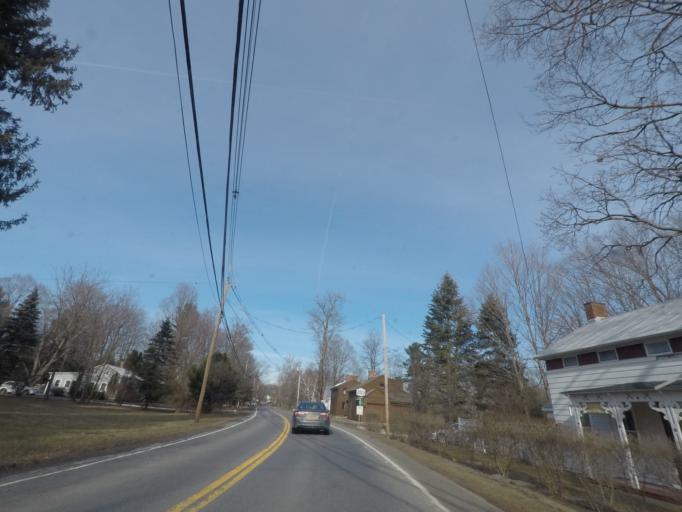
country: US
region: New York
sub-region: Columbia County
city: Niverville
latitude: 42.4667
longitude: -73.6326
